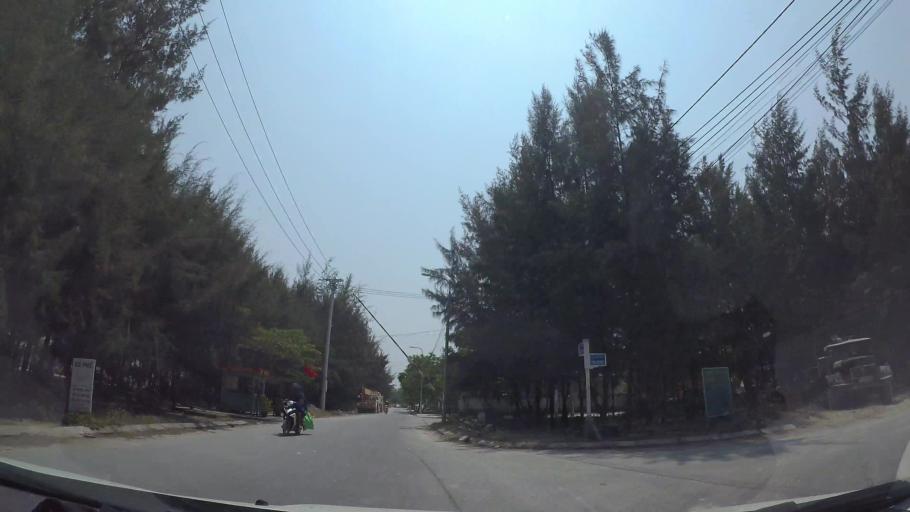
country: VN
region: Da Nang
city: Ngu Hanh Son
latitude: 15.9928
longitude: 108.2533
